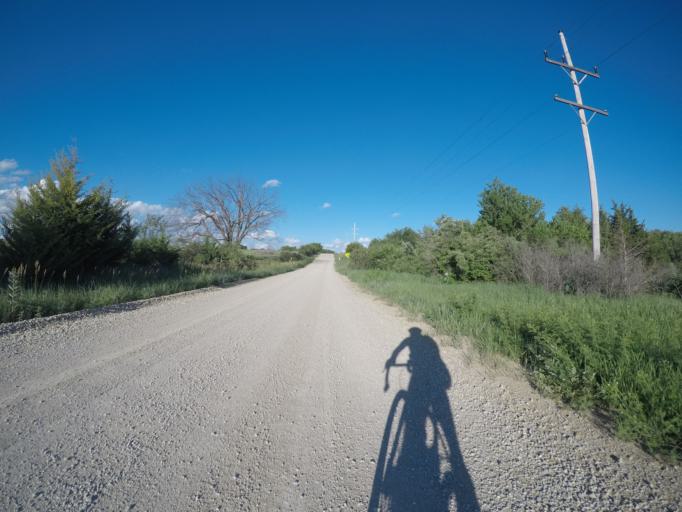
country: US
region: Kansas
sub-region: Riley County
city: Ogden
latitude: 39.2618
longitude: -96.7030
